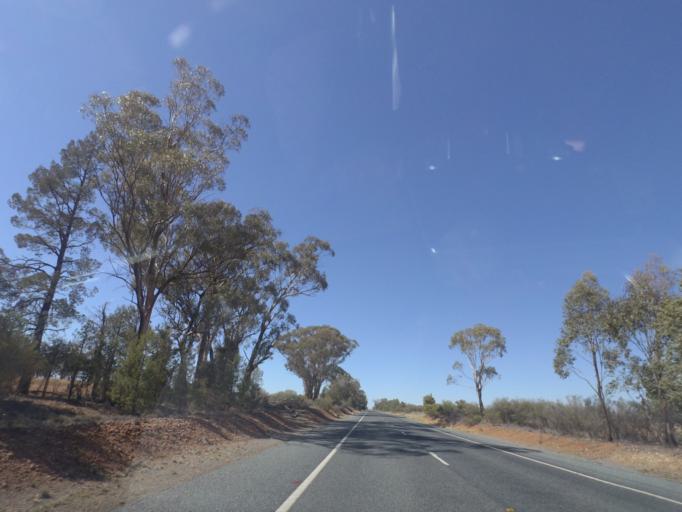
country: AU
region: New South Wales
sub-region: Bland
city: West Wyalong
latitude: -34.1611
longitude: 147.1167
